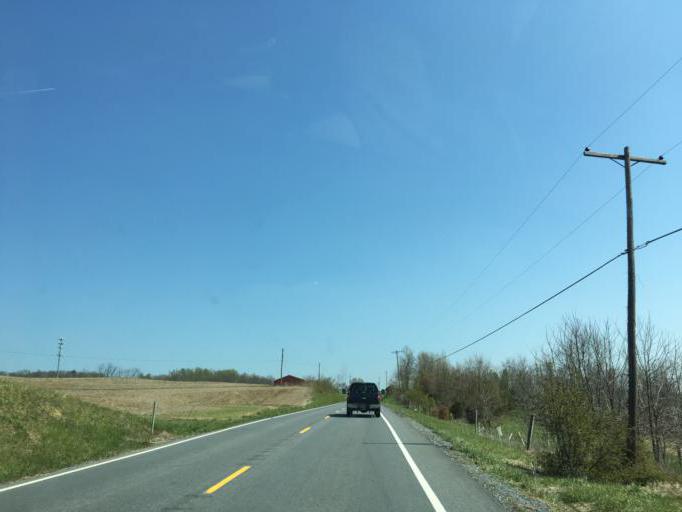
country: US
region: Maryland
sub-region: Frederick County
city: Woodsboro
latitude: 39.4960
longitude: -77.2581
